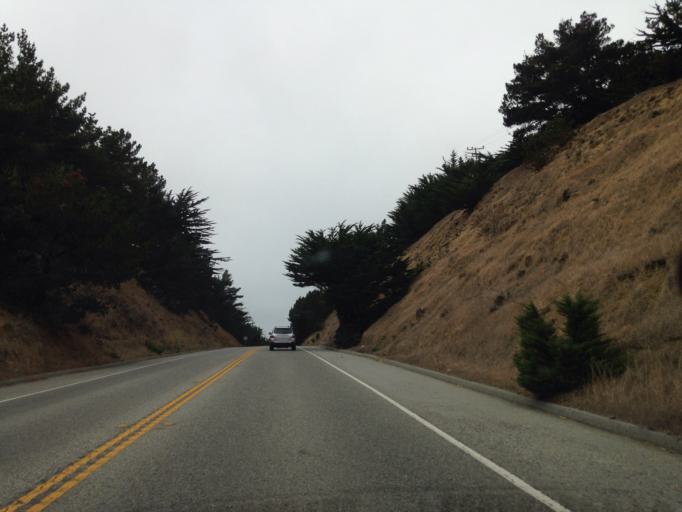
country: US
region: California
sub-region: San Mateo County
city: Half Moon Bay
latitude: 37.3620
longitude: -122.4012
